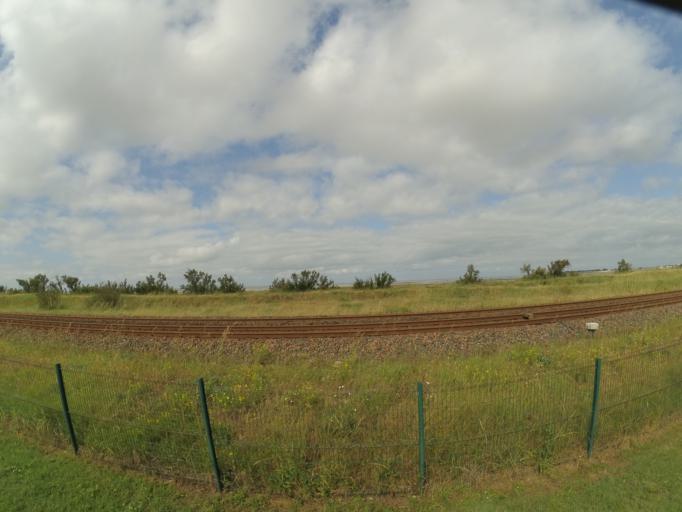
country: FR
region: Poitou-Charentes
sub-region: Departement de la Charente-Maritime
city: Angoulins
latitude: 46.0914
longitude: -1.0992
